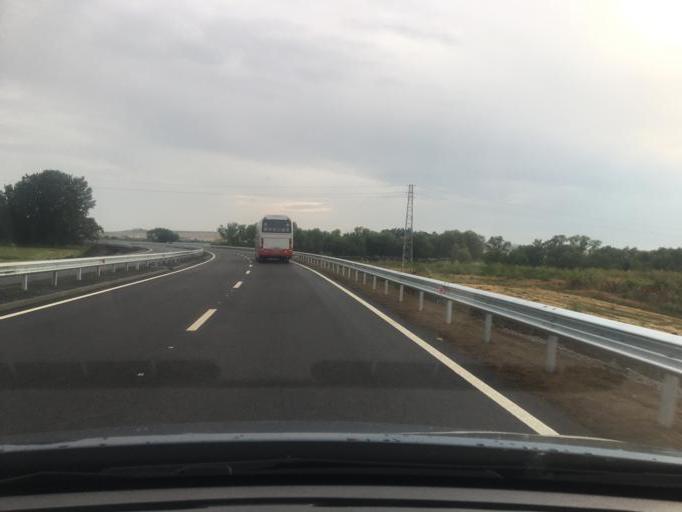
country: BG
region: Burgas
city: Aheloy
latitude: 42.6539
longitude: 27.6405
